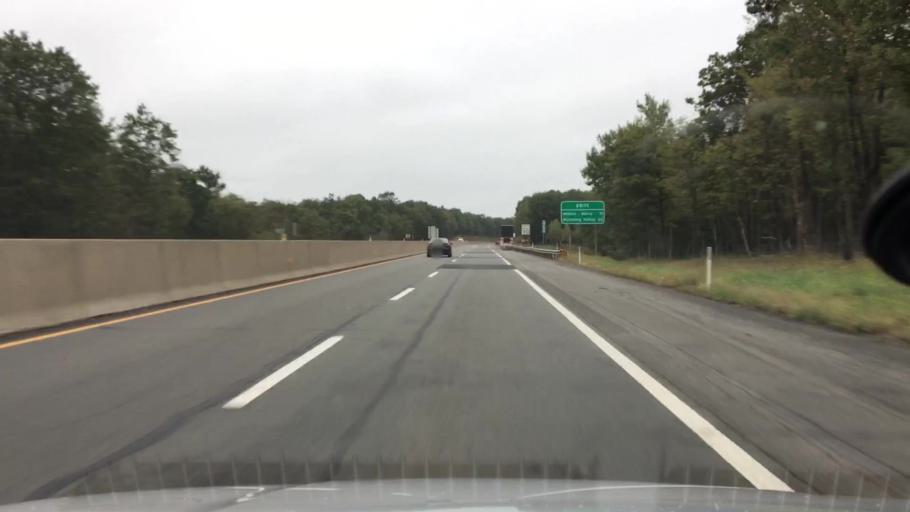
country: US
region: Pennsylvania
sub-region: Luzerne County
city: White Haven
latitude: 41.0762
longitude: -75.7201
